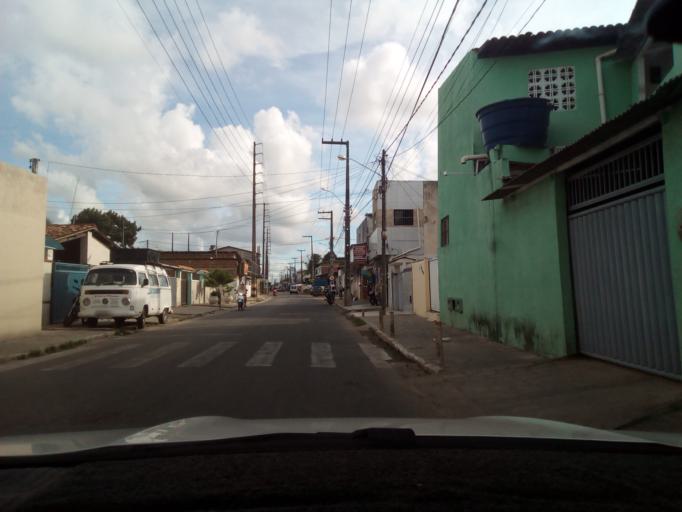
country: BR
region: Paraiba
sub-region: Joao Pessoa
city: Joao Pessoa
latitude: -7.1604
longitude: -34.8790
